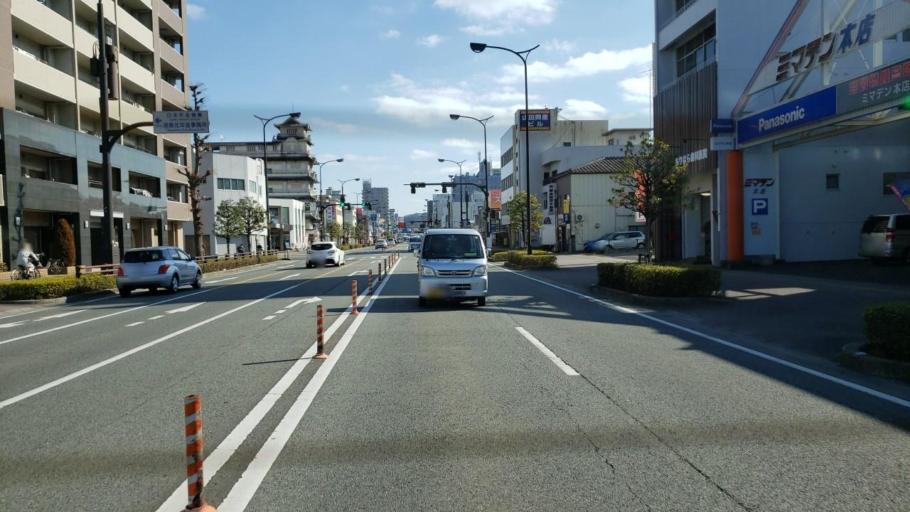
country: JP
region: Tokushima
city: Tokushima-shi
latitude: 34.0783
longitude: 134.5339
